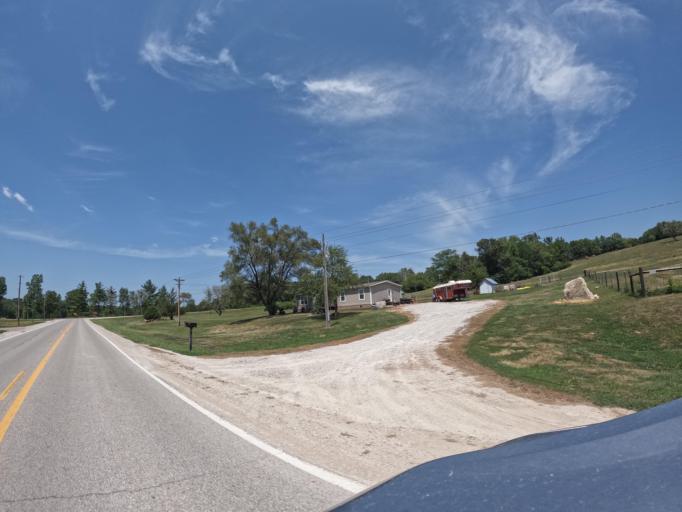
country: US
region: Iowa
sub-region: Henry County
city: Mount Pleasant
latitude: 40.9386
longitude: -91.6155
